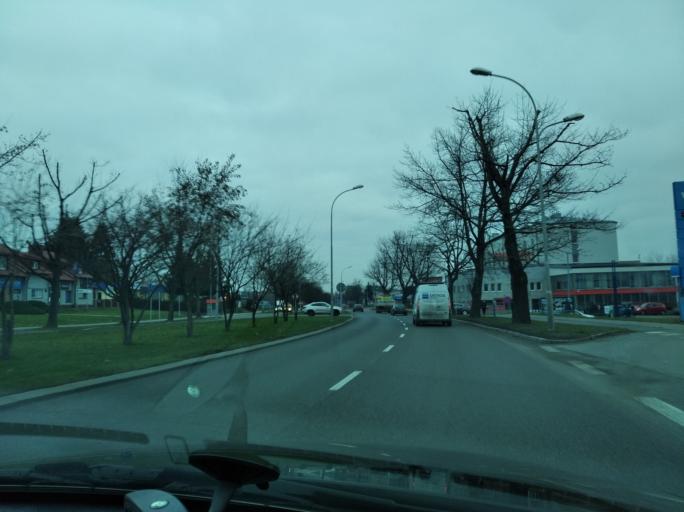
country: PL
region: Subcarpathian Voivodeship
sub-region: Rzeszow
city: Rzeszow
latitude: 50.0510
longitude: 21.9892
